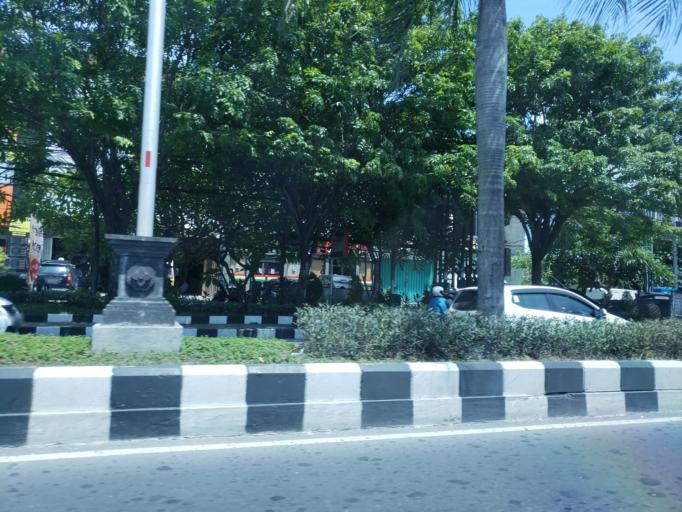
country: ID
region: Bali
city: Jabajero
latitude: -8.7394
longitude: 115.1802
